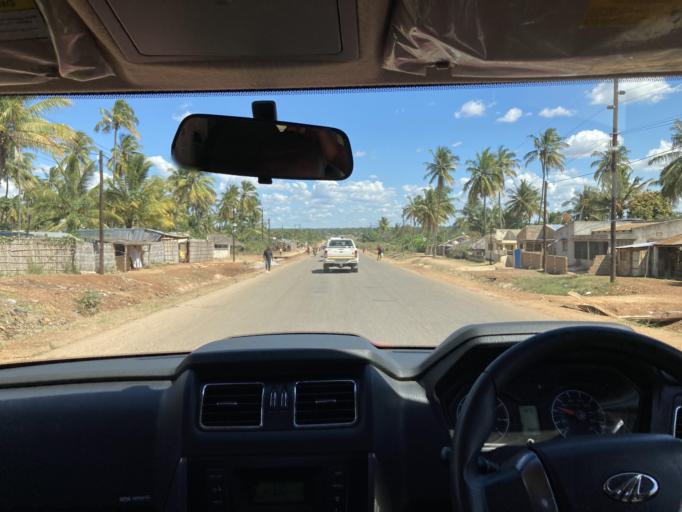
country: MZ
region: Cabo Delgado
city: Montepuez
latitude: -13.1331
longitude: 38.9924
